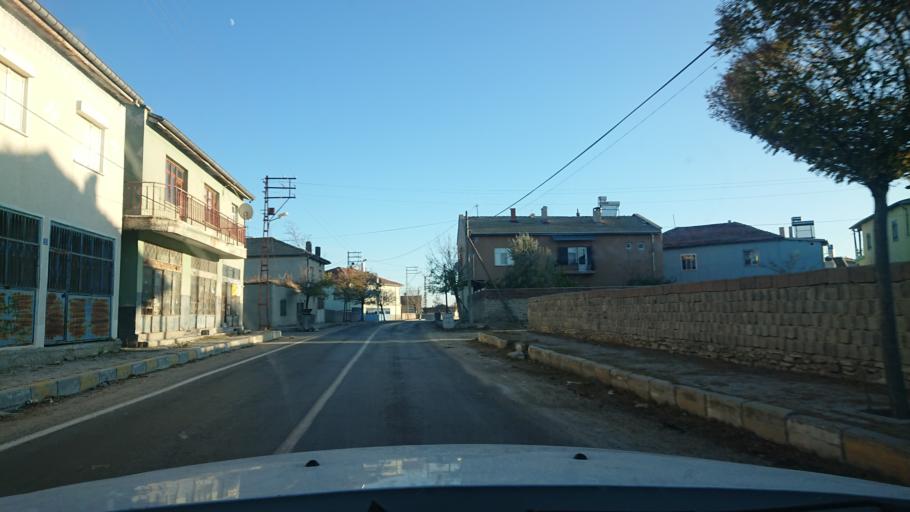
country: TR
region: Aksaray
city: Eskil
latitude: 38.5576
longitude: 33.1993
